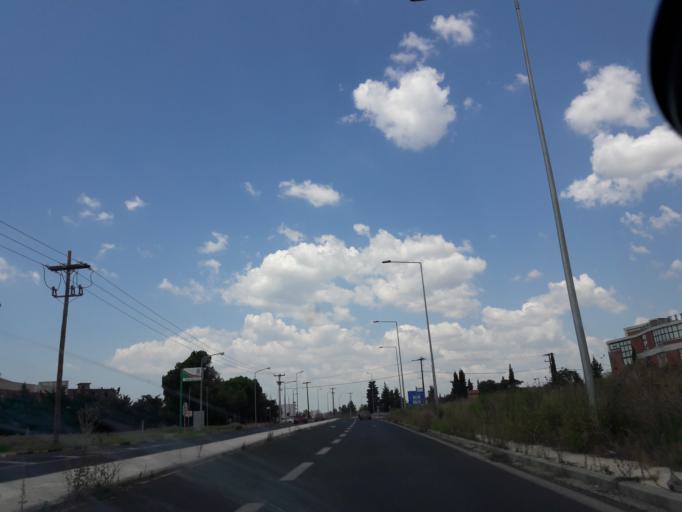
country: GR
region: Central Macedonia
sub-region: Nomos Thessalonikis
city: Thermi
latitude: 40.5323
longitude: 23.0403
